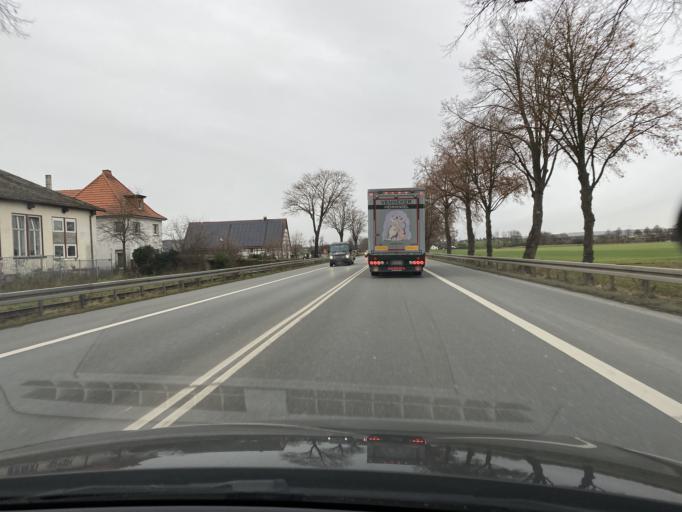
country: DE
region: North Rhine-Westphalia
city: Erwitte
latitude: 51.6375
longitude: 8.3420
